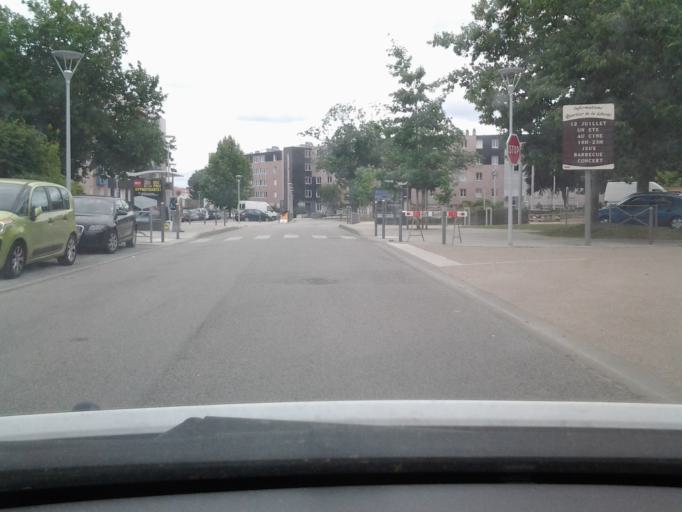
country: FR
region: Pays de la Loire
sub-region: Departement de la Vendee
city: La Roche-sur-Yon
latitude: 46.6628
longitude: -1.4345
